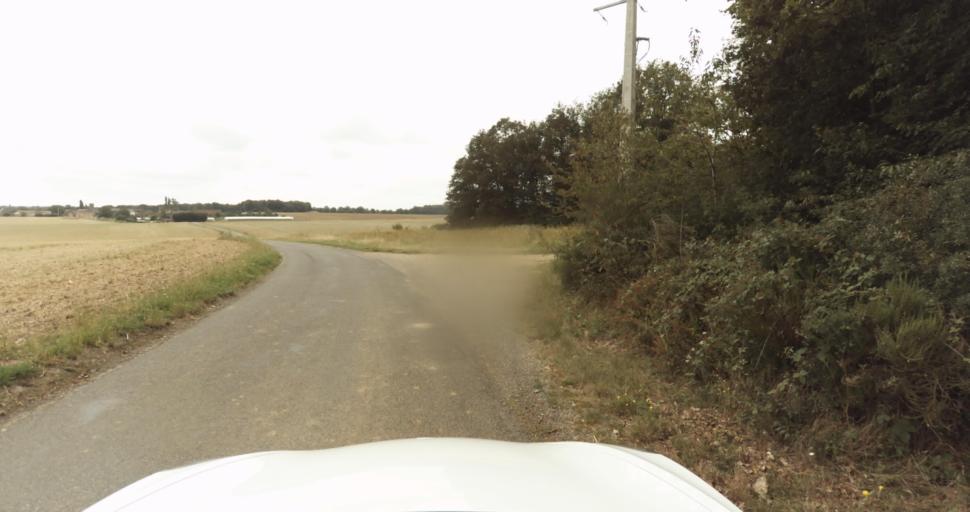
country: FR
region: Haute-Normandie
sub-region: Departement de l'Eure
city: Saint-Sebastien-de-Morsent
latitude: 49.0239
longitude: 1.0613
